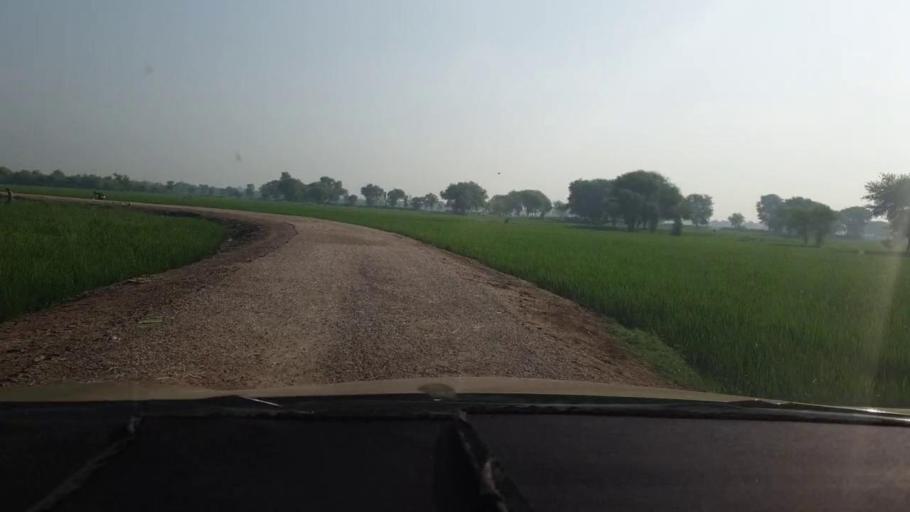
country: PK
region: Sindh
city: Kambar
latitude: 27.5952
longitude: 68.1097
